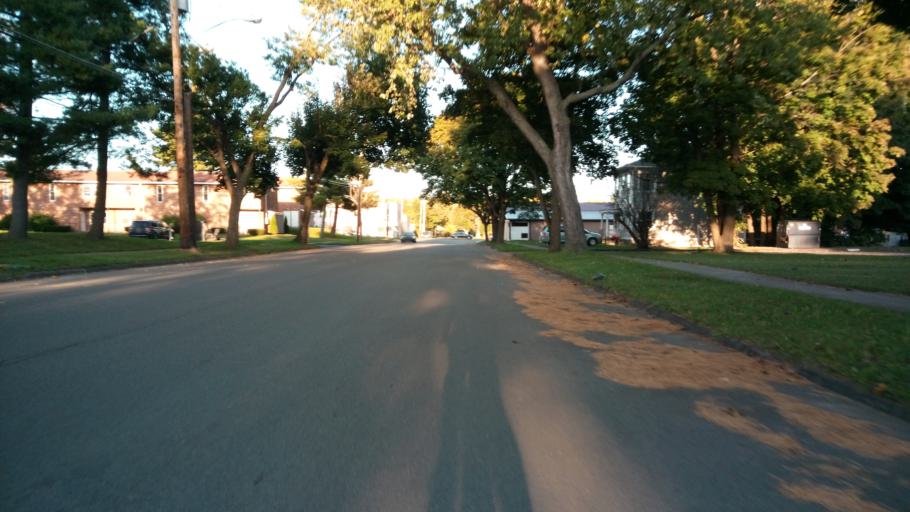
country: US
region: New York
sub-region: Chemung County
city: Elmira
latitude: 42.0842
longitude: -76.8076
